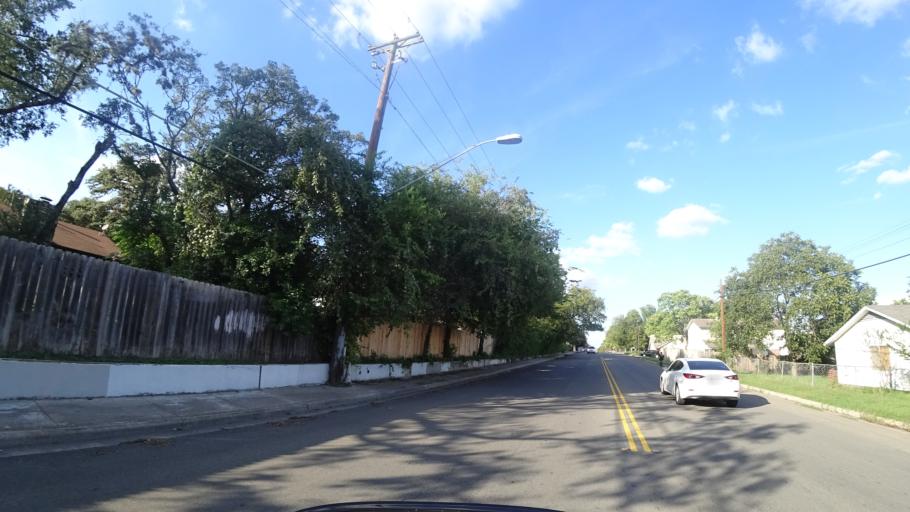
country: US
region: Texas
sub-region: Travis County
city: Onion Creek
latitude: 30.1965
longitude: -97.7924
